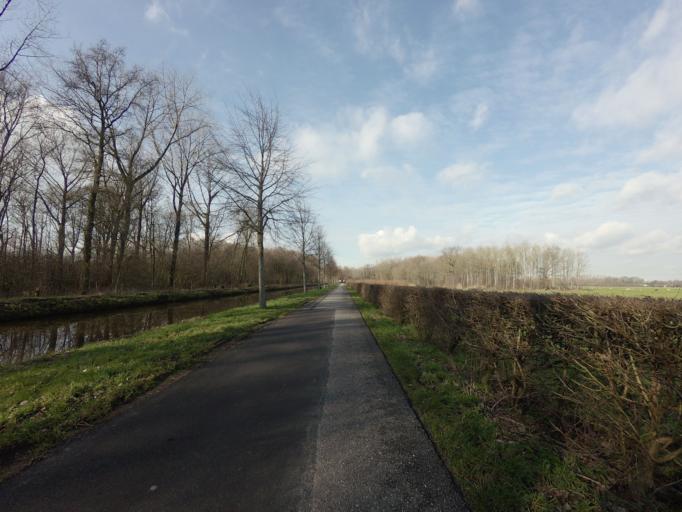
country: NL
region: Utrecht
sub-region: Gemeente Woerden
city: Woerden
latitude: 52.0615
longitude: 4.9015
